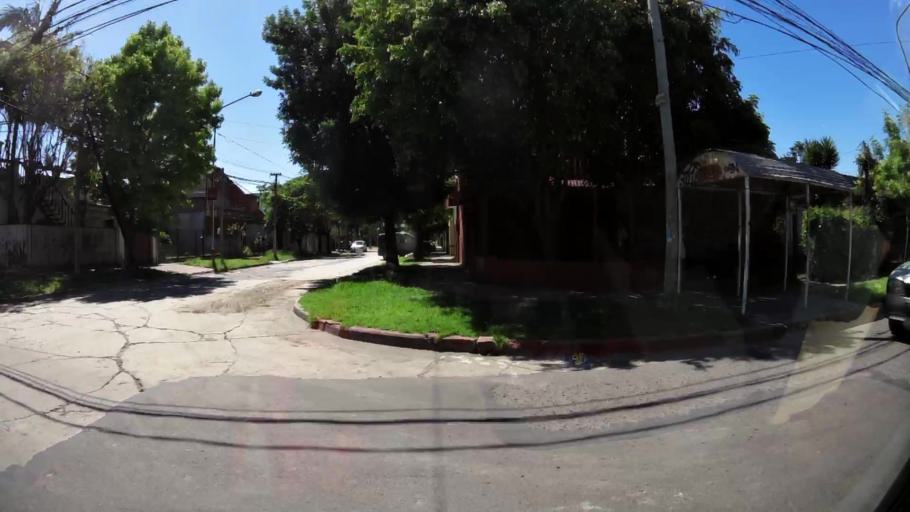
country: AR
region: Buenos Aires
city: Ituzaingo
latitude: -34.6663
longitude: -58.6599
